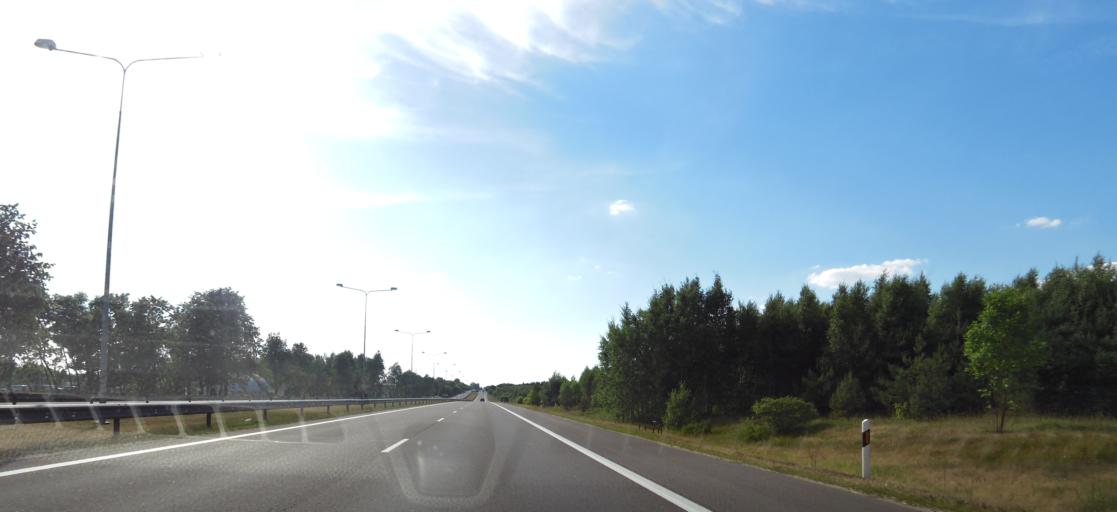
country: LT
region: Vilnius County
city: Rasos
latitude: 54.6462
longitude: 25.3324
